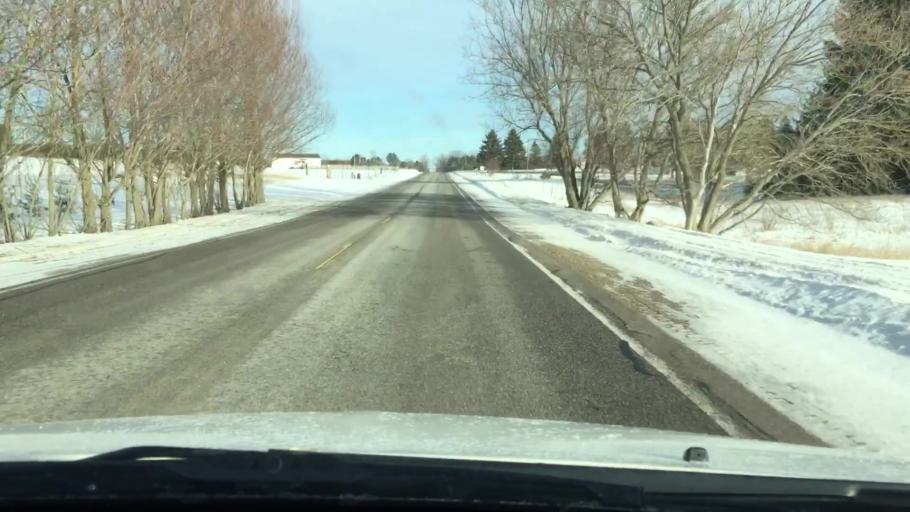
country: US
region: Michigan
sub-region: Kalkaska County
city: Kalkaska
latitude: 44.6404
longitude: -85.2012
